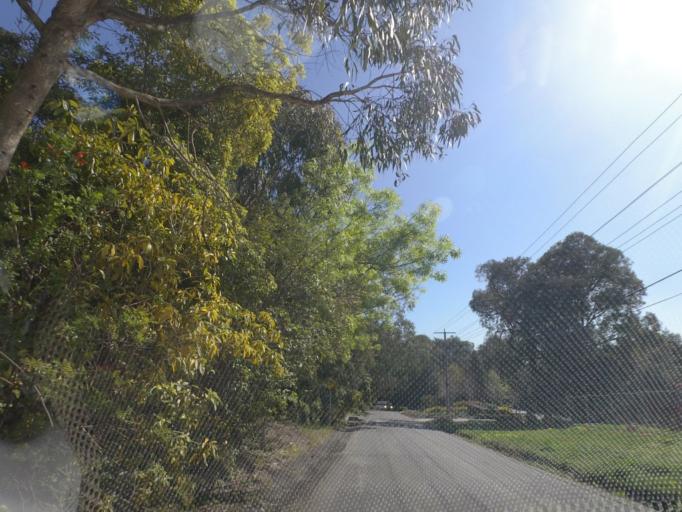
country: AU
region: Victoria
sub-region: Manningham
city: Park Orchards
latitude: -37.7894
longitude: 145.2294
